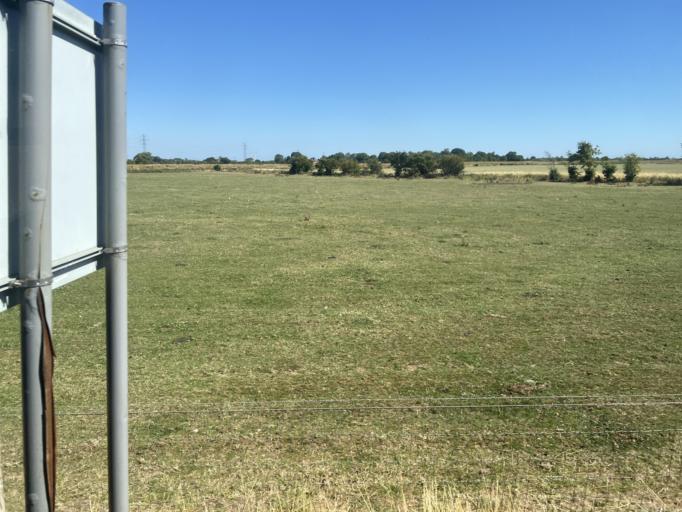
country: GB
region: England
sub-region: Lincolnshire
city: Wainfleet All Saints
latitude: 53.1183
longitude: 0.2067
